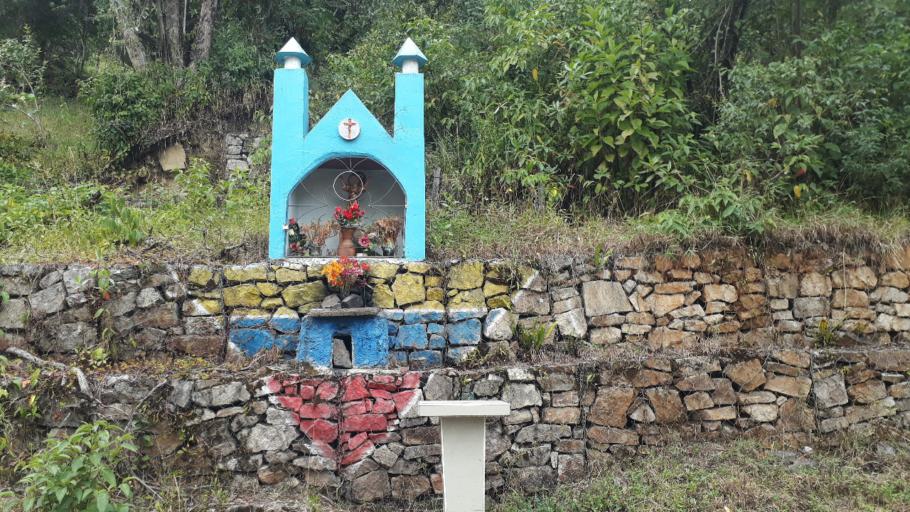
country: CO
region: Boyaca
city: San Mateo
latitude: 6.3952
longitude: -72.5568
